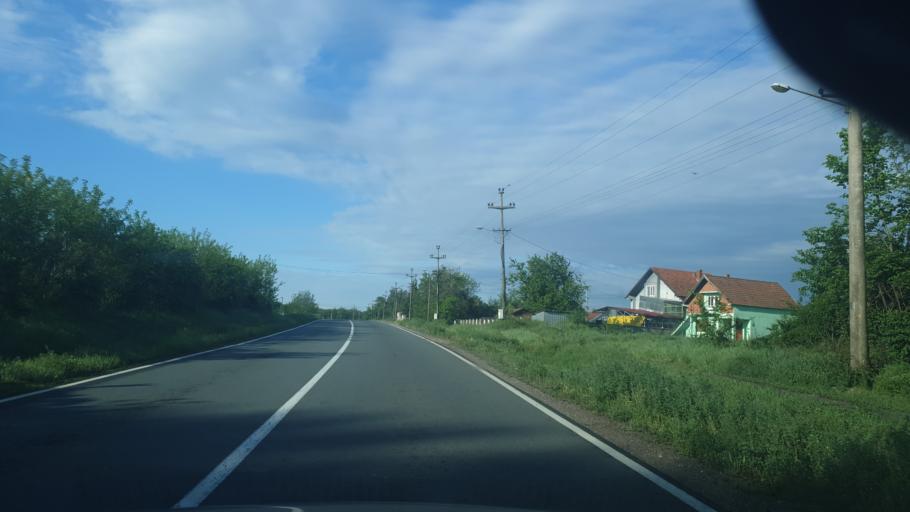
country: RS
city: Stubline
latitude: 44.6047
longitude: 20.1506
